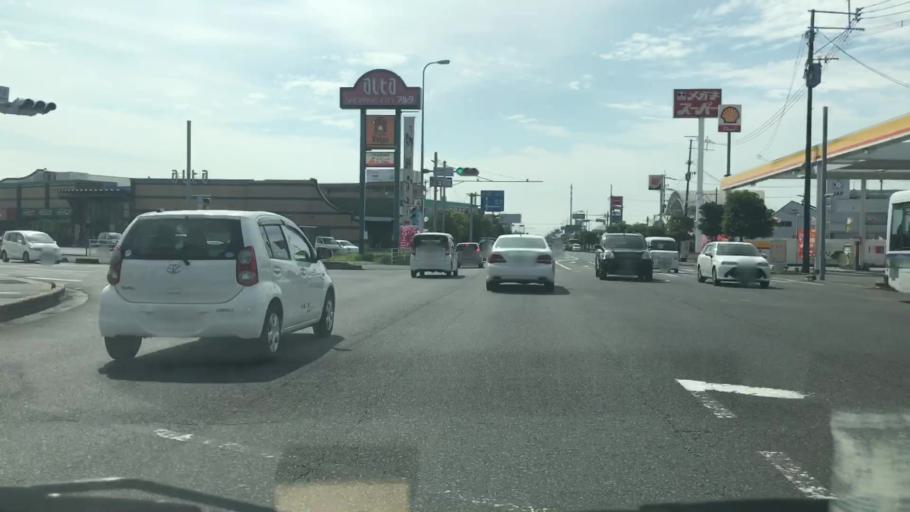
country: JP
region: Saga Prefecture
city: Saga-shi
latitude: 33.2931
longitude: 130.2850
